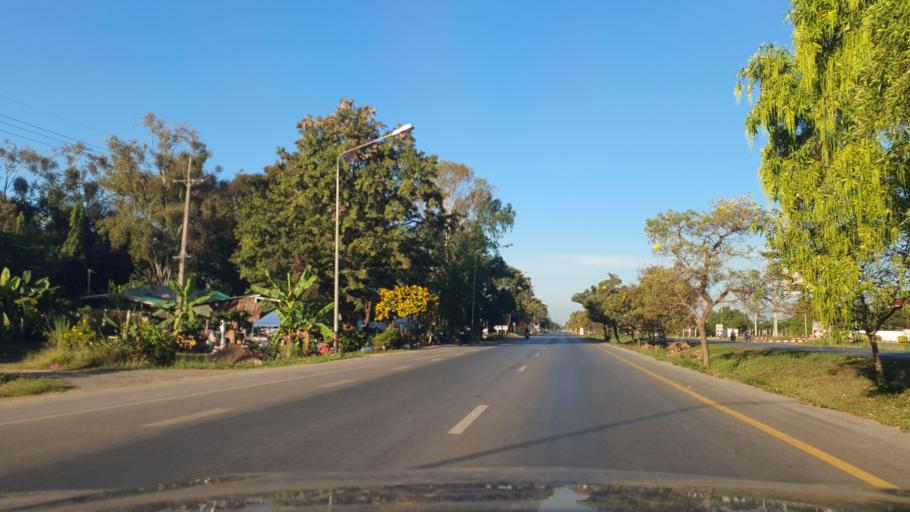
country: TH
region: Phitsanulok
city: Phitsanulok
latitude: 16.8649
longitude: 100.2406
